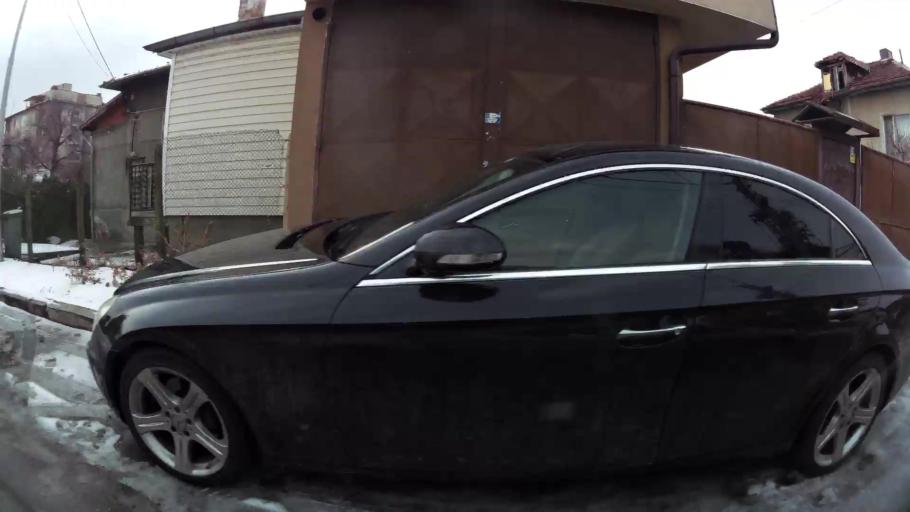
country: BG
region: Sofia-Capital
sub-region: Stolichna Obshtina
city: Sofia
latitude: 42.6993
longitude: 23.3795
